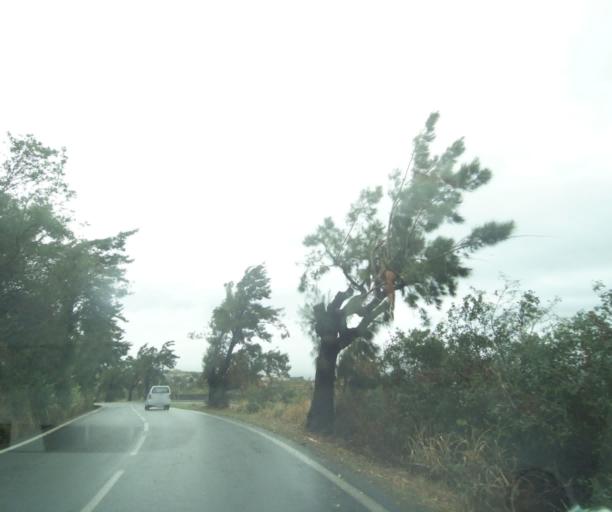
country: RE
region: Reunion
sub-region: Reunion
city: Saint-Paul
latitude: -21.0318
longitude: 55.2828
